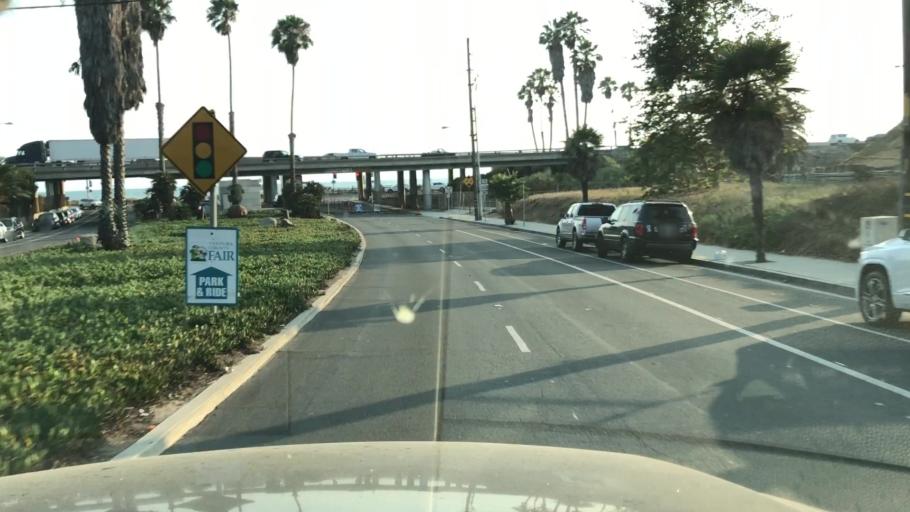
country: US
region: California
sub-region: Ventura County
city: Ventura
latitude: 34.2741
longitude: -119.2837
